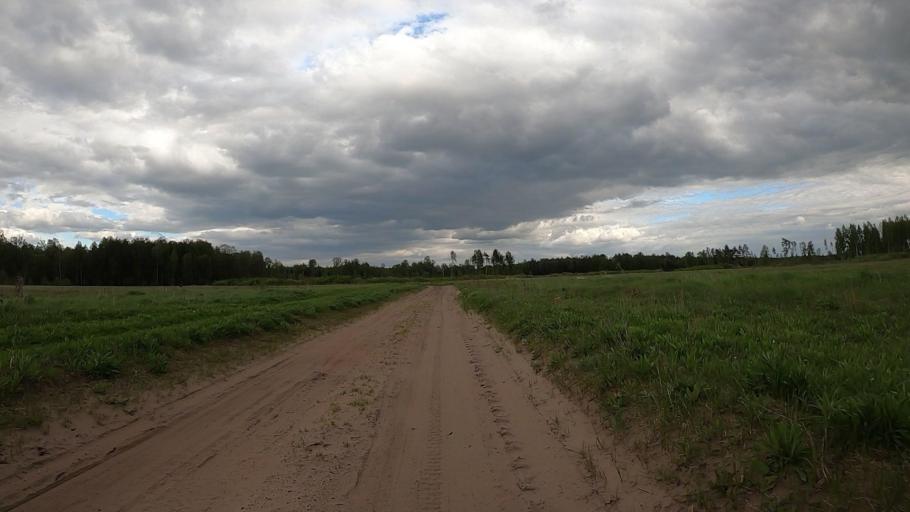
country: LV
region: Ozolnieku
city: Ozolnieki
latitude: 56.8135
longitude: 23.7764
